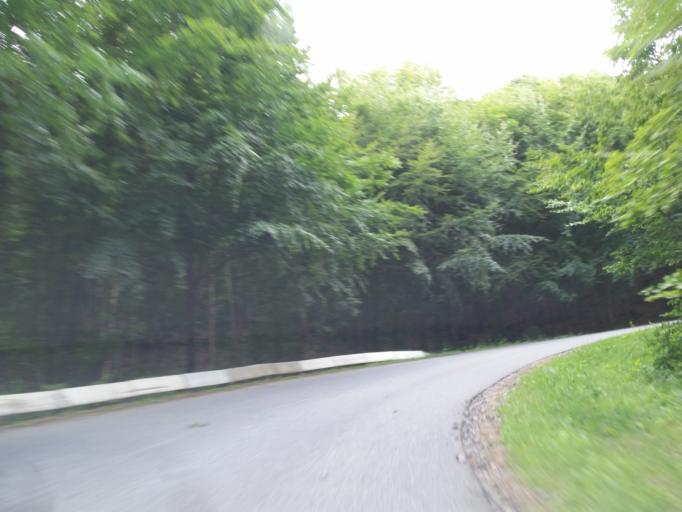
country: DK
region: South Denmark
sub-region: Vejle Kommune
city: Borkop
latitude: 55.6890
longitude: 9.6196
